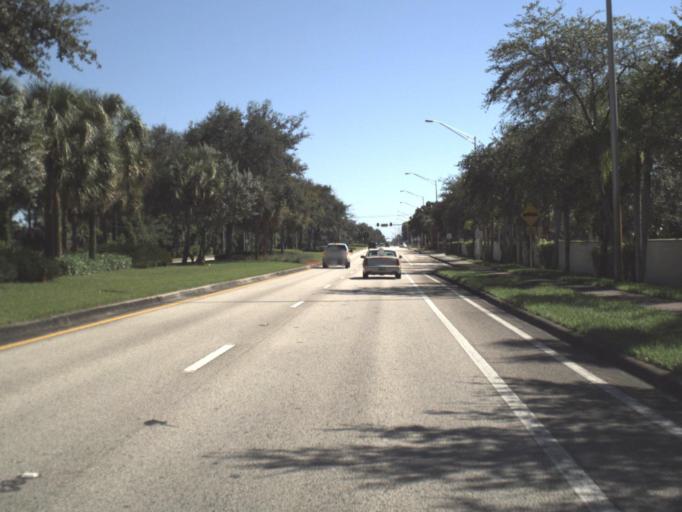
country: US
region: Florida
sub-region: Collier County
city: Naples
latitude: 26.1386
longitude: -81.7531
